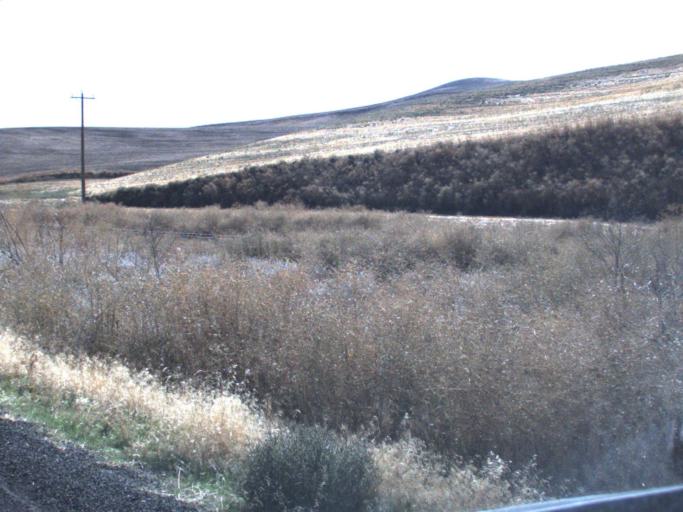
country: US
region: Washington
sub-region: Walla Walla County
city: Walla Walla
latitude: 46.2103
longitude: -118.3899
